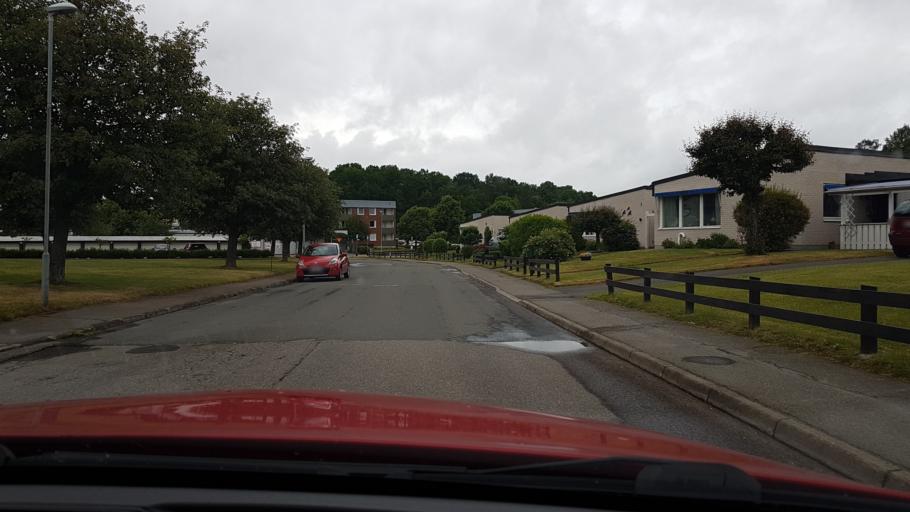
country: SE
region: Vaestra Goetaland
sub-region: Skovde Kommun
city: Skultorp
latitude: 58.3677
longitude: 13.8245
